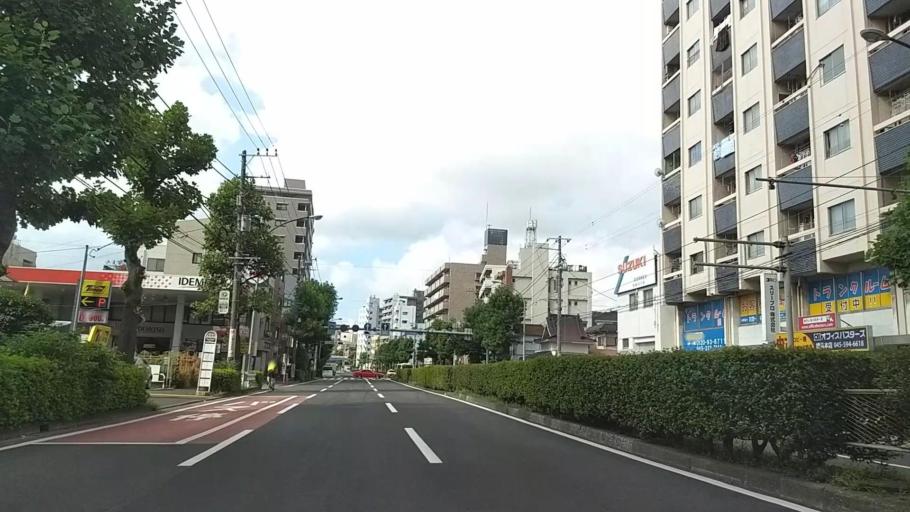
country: JP
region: Kanagawa
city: Yokohama
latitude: 35.4631
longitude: 139.6102
